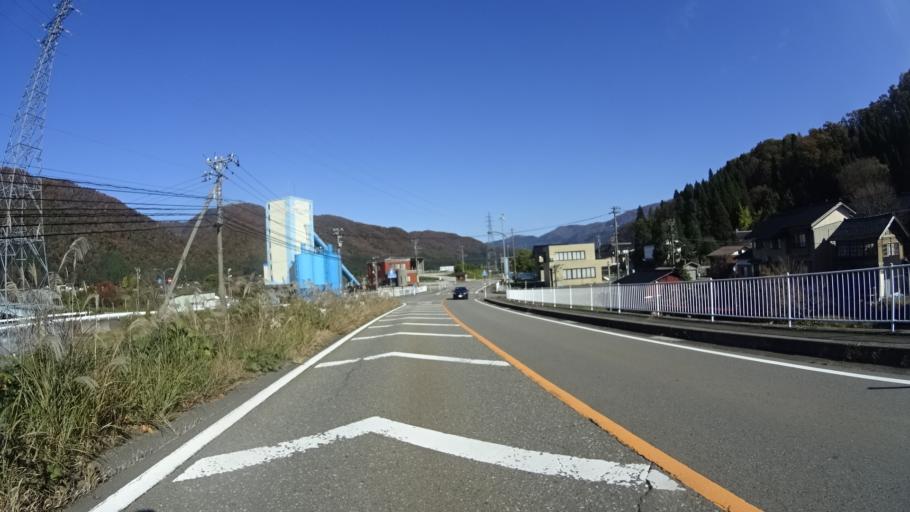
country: JP
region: Ishikawa
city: Tsurugi-asahimachi
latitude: 36.3861
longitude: 136.6124
